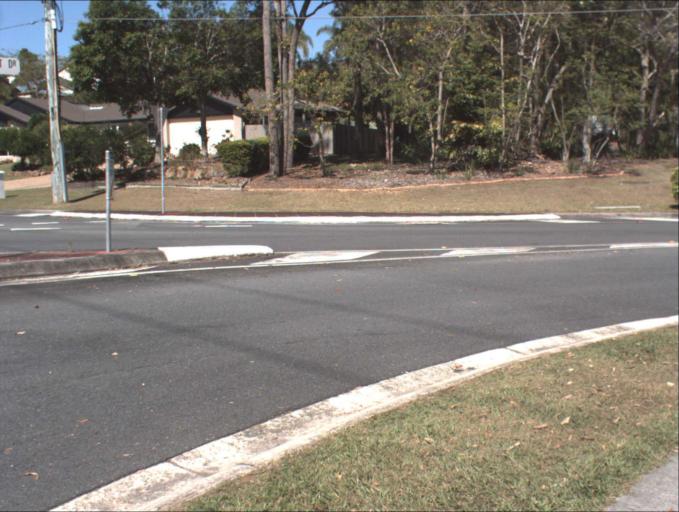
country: AU
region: Queensland
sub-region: Logan
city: Springwood
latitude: -27.6129
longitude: 153.1427
